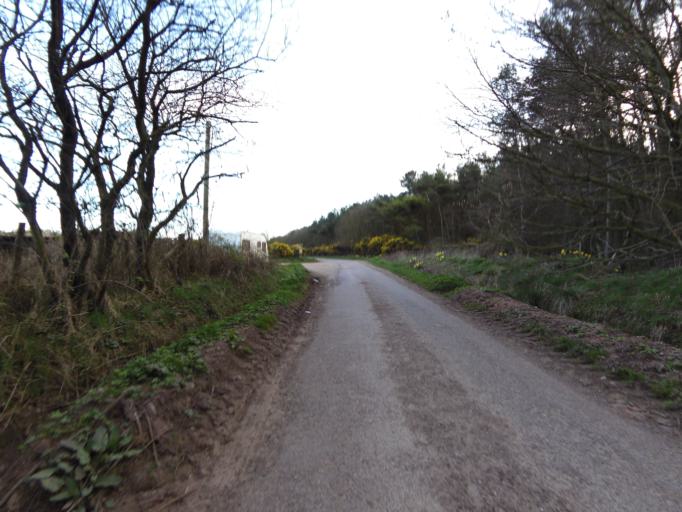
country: GB
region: Scotland
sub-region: Aberdeenshire
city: Stonehaven
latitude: 56.9268
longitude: -2.2287
